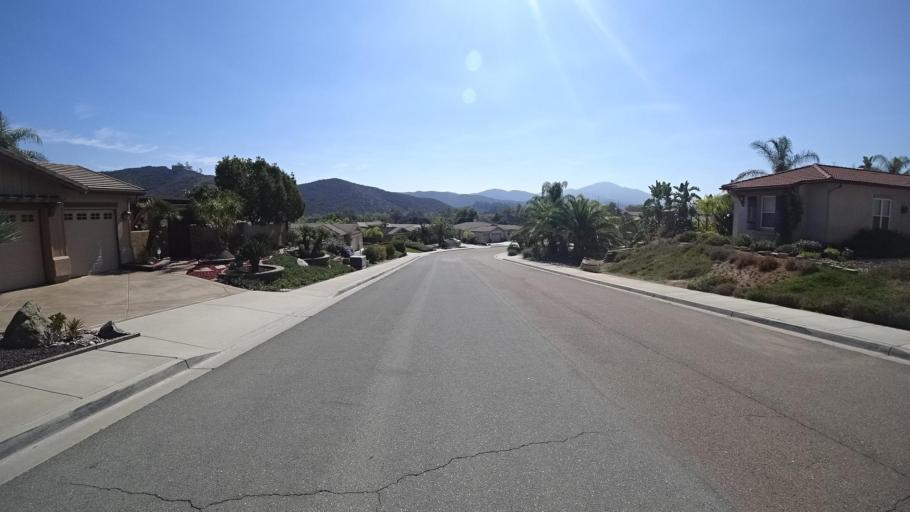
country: US
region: California
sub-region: San Diego County
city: Rancho San Diego
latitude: 32.7601
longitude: -116.9005
